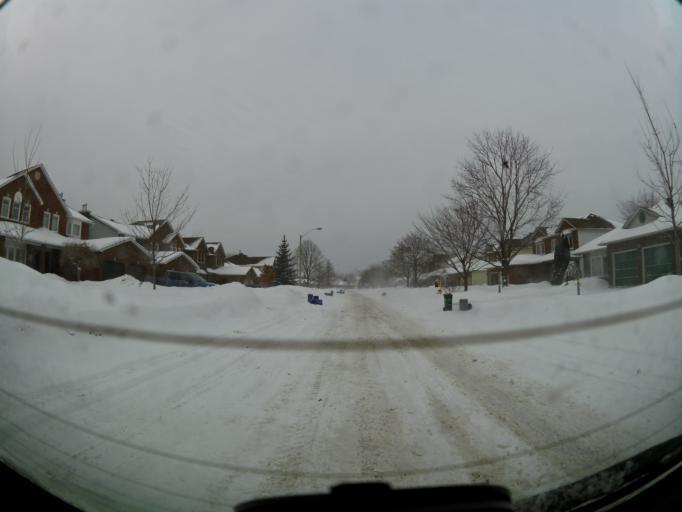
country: CA
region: Ontario
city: Ottawa
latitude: 45.3746
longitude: -75.6135
